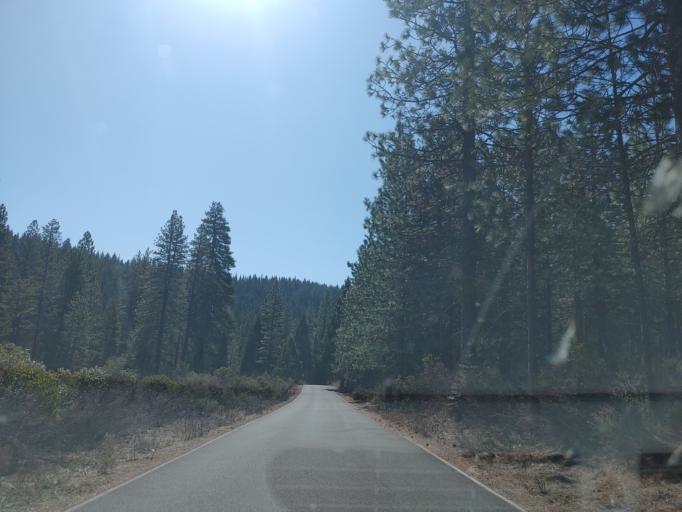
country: US
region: California
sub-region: Siskiyou County
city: McCloud
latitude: 41.2437
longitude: -122.0274
